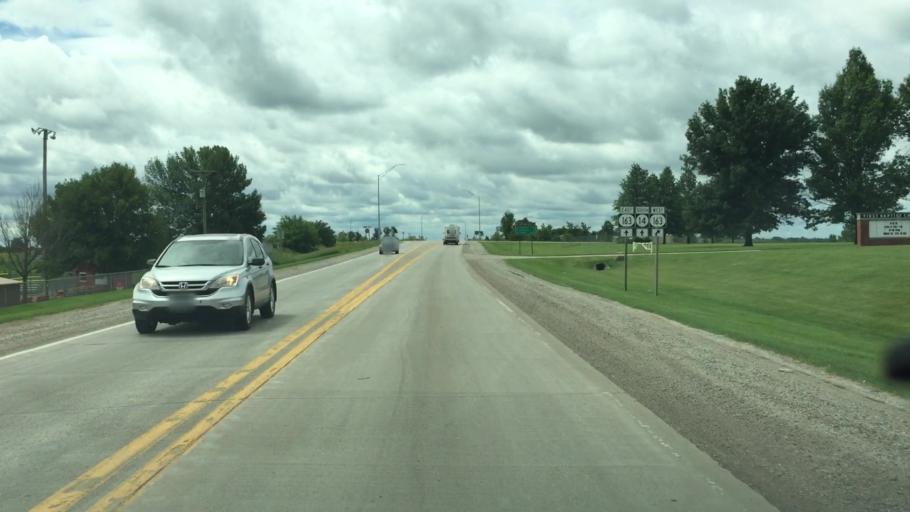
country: US
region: Iowa
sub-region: Jasper County
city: Monroe
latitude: 41.5145
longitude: -93.1015
